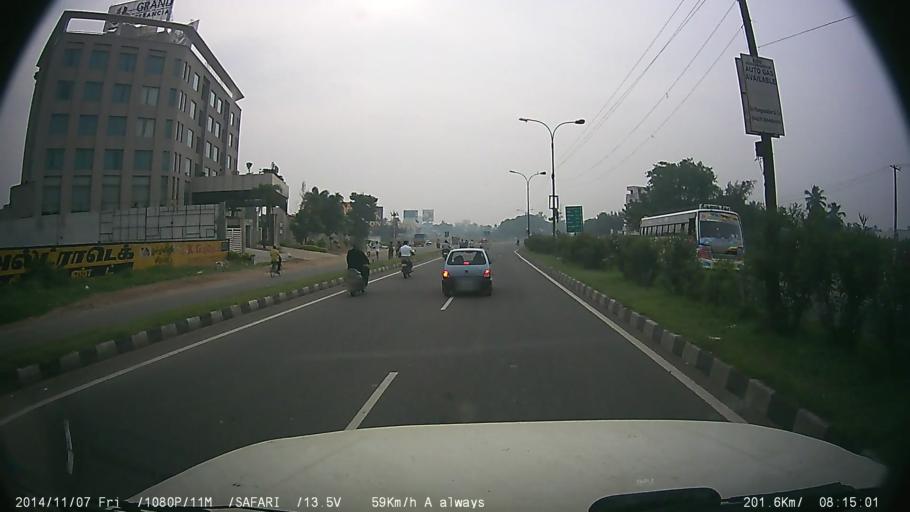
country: IN
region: Tamil Nadu
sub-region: Salem
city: Salem
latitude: 11.6837
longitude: 78.1245
